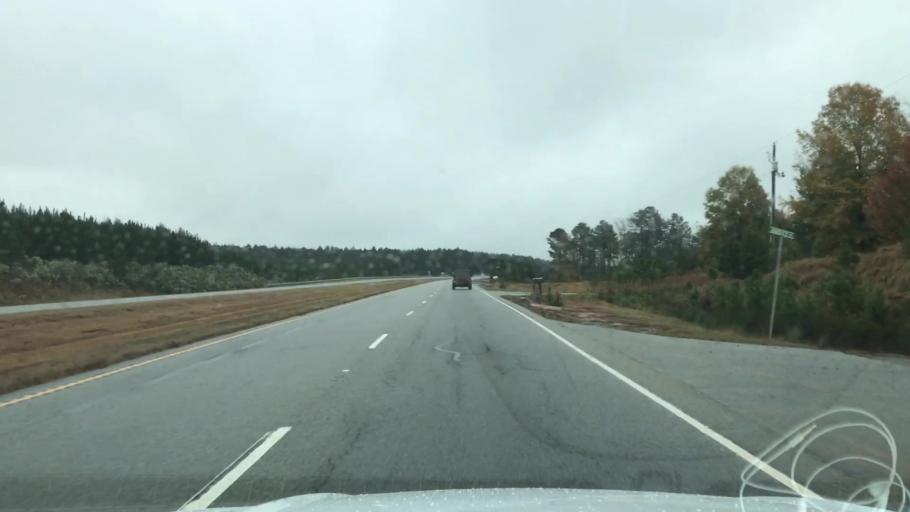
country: US
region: South Carolina
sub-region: Greenwood County
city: Ninety Six
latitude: 34.3344
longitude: -81.9836
